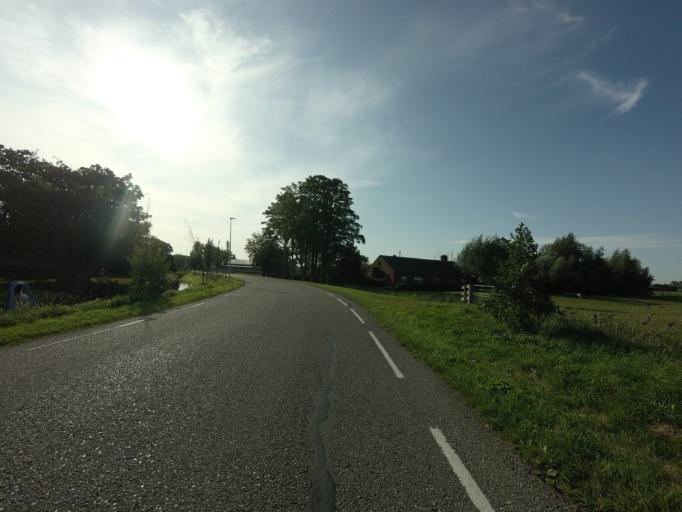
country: NL
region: Utrecht
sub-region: Gemeente Lopik
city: Lopik
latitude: 51.9467
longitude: 4.9660
